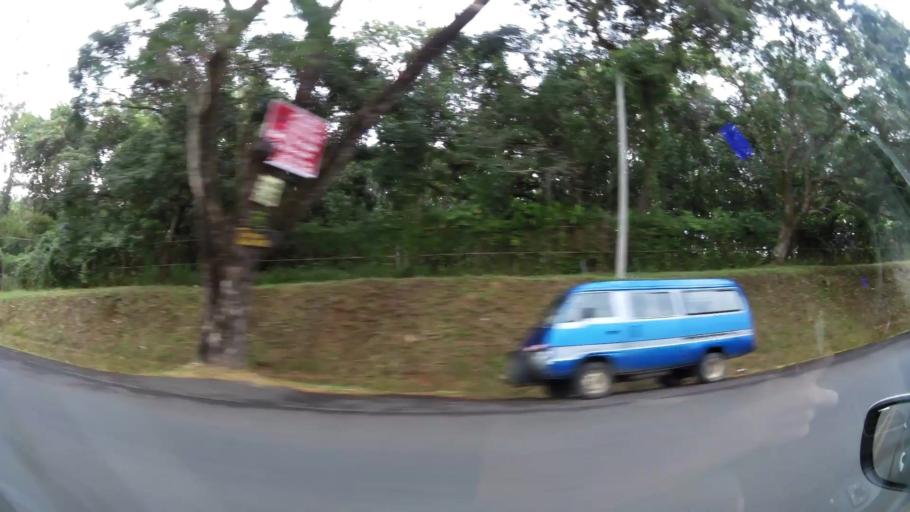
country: CR
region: Alajuela
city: Orotina
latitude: 9.9256
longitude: -84.5207
